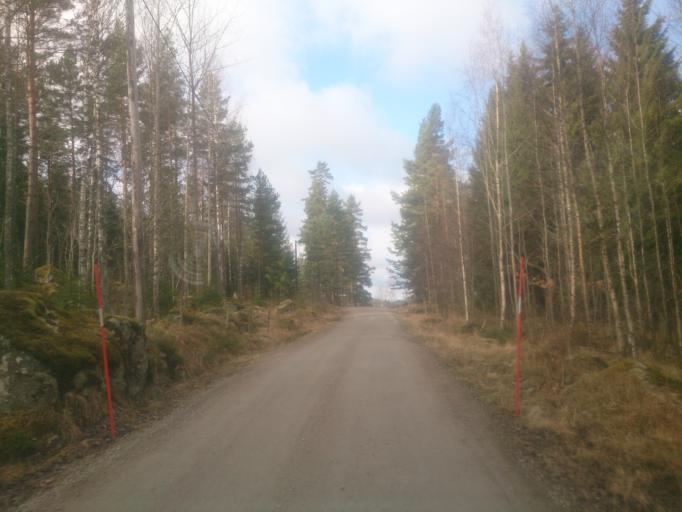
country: SE
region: OEstergoetland
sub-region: Atvidabergs Kommun
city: Atvidaberg
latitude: 58.2227
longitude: 16.1725
